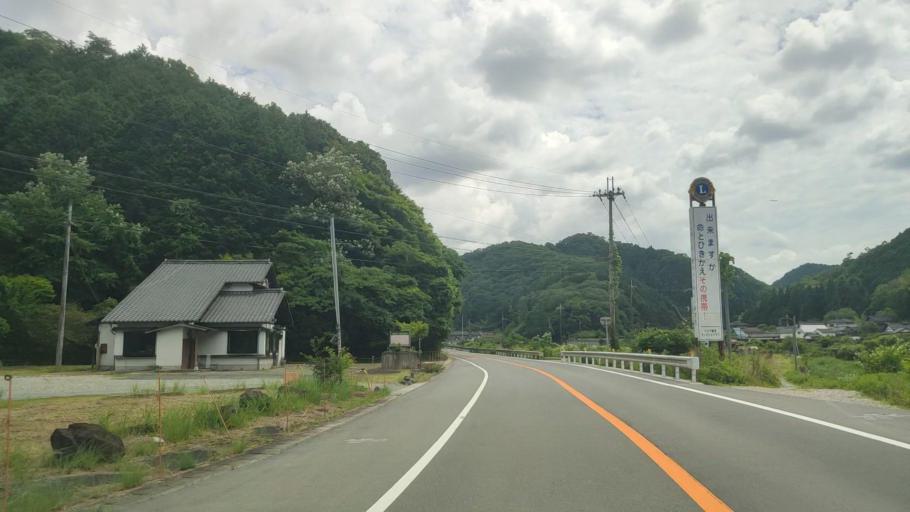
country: JP
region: Hyogo
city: Yamazakicho-nakabirose
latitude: 34.9676
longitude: 134.4476
